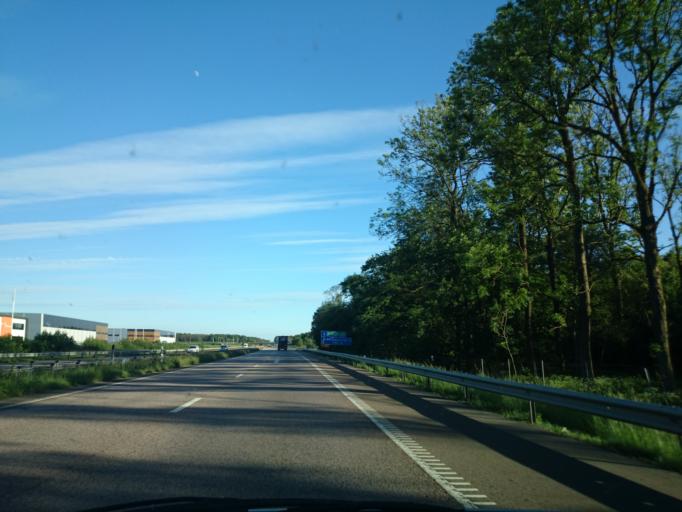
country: SE
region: Skane
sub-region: Helsingborg
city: Odakra
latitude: 56.0726
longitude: 12.7785
